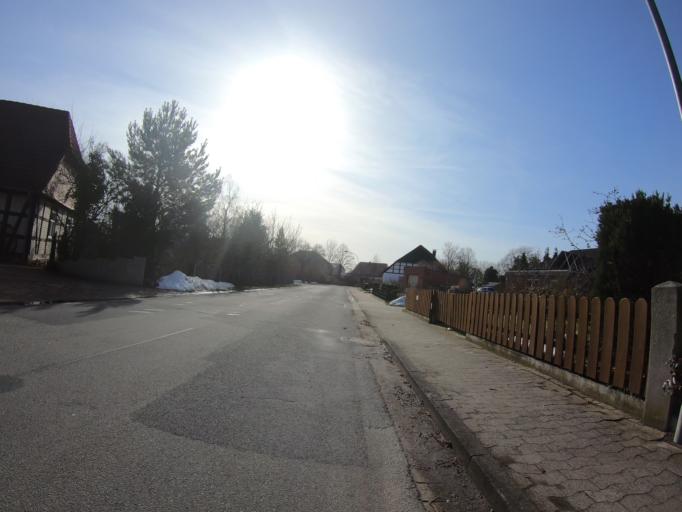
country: DE
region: Lower Saxony
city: Wasbuttel
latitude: 52.4079
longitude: 10.5643
